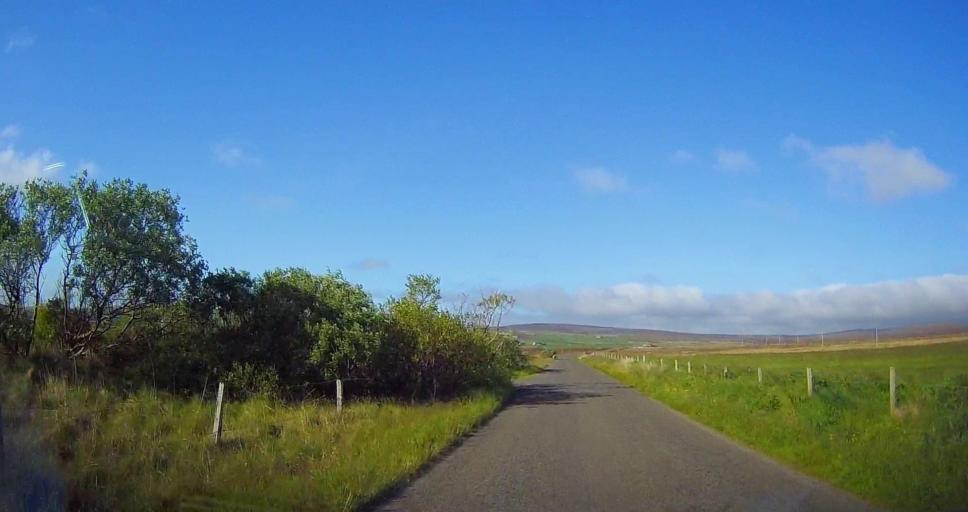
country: GB
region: Scotland
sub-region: Orkney Islands
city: Stromness
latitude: 59.0771
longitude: -3.2027
